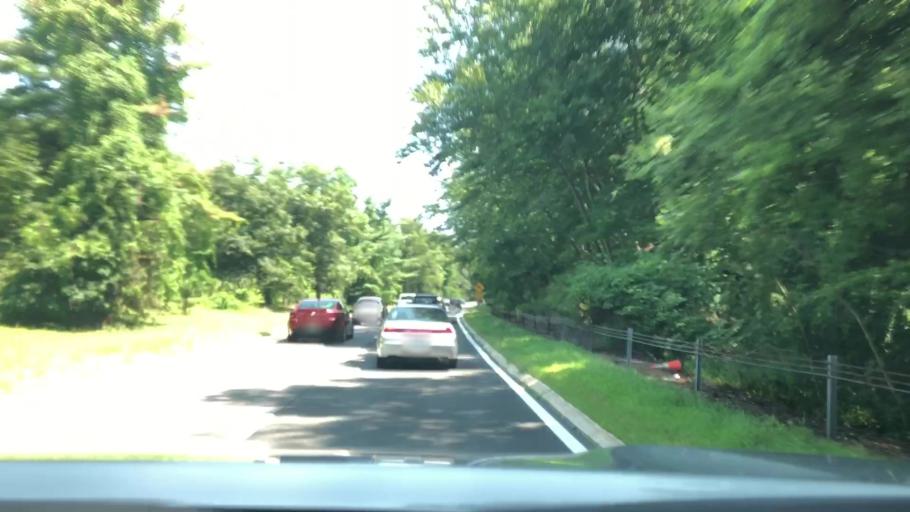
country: US
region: New York
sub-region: Rockland County
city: Thiells
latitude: 41.2632
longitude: -74.0401
